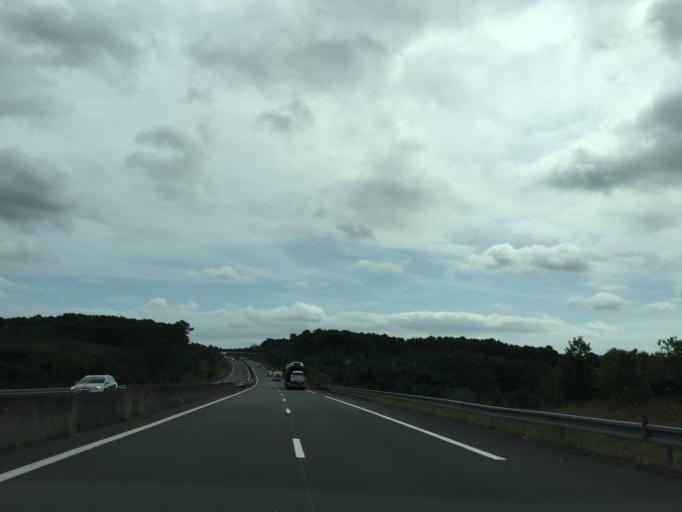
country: FR
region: Pays de la Loire
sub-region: Departement de la Sarthe
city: Mayet
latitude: 47.7486
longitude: 0.3160
